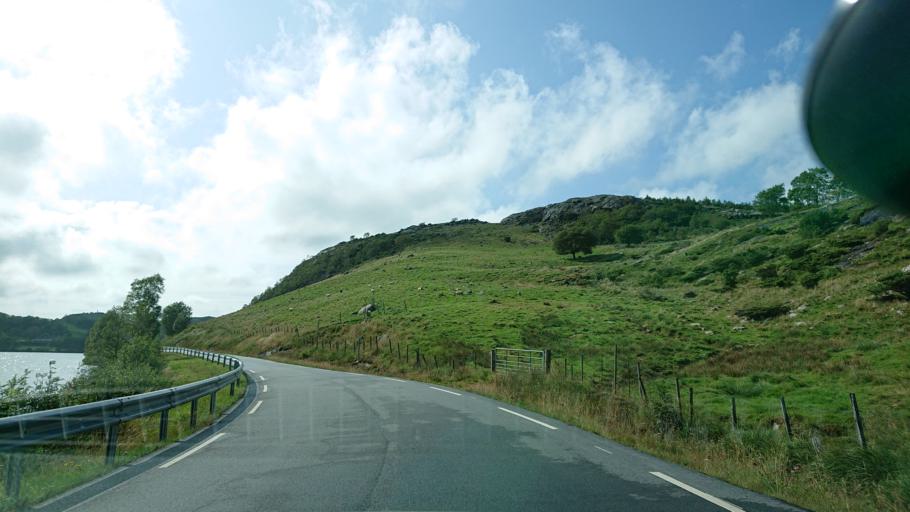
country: NO
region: Rogaland
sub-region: Gjesdal
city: Algard
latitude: 58.6774
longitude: 5.8374
